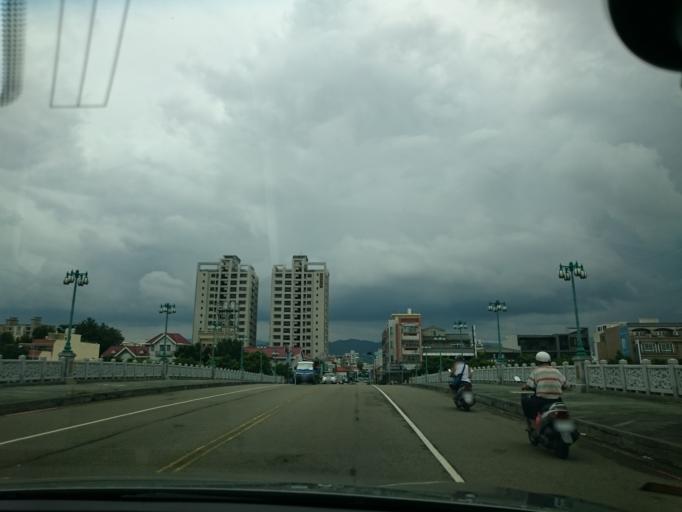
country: TW
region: Taiwan
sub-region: Taichung City
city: Taichung
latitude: 24.1401
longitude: 120.7005
